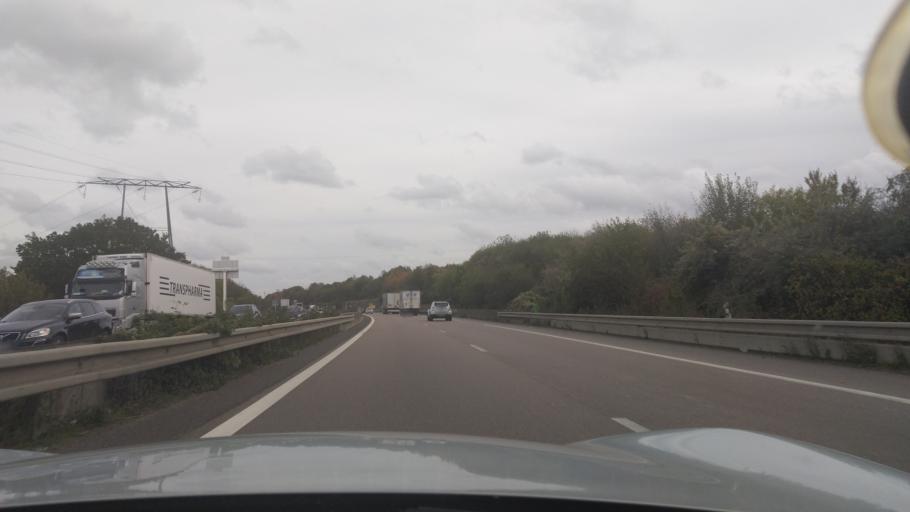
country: FR
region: Ile-de-France
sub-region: Departement du Val-d'Oise
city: Louvres
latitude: 49.0346
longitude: 2.4880
